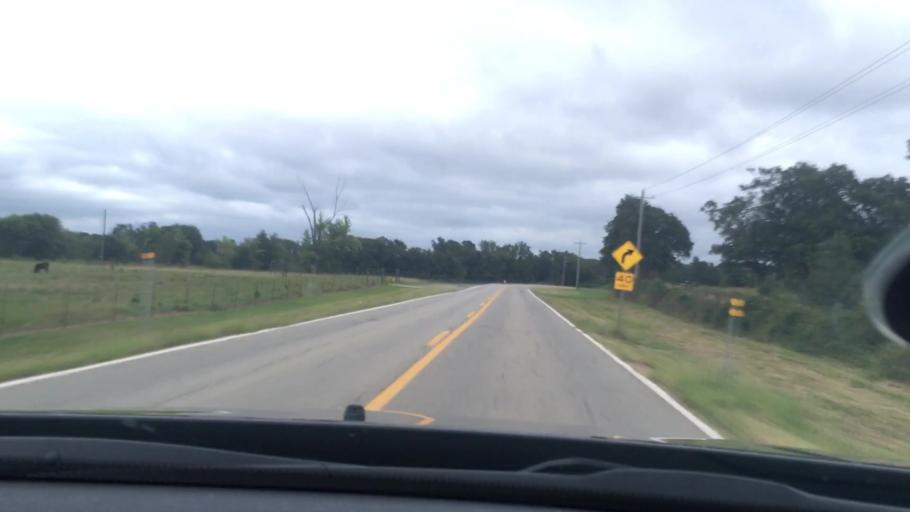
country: US
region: Oklahoma
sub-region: Sequoyah County
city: Vian
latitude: 35.6077
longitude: -94.9993
